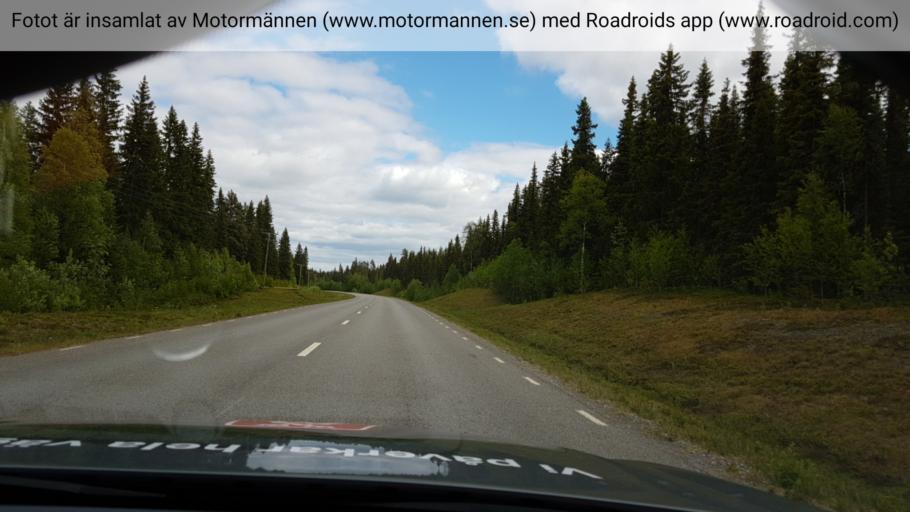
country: SE
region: Jaemtland
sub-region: Stroemsunds Kommun
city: Stroemsund
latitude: 64.2273
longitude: 15.5027
